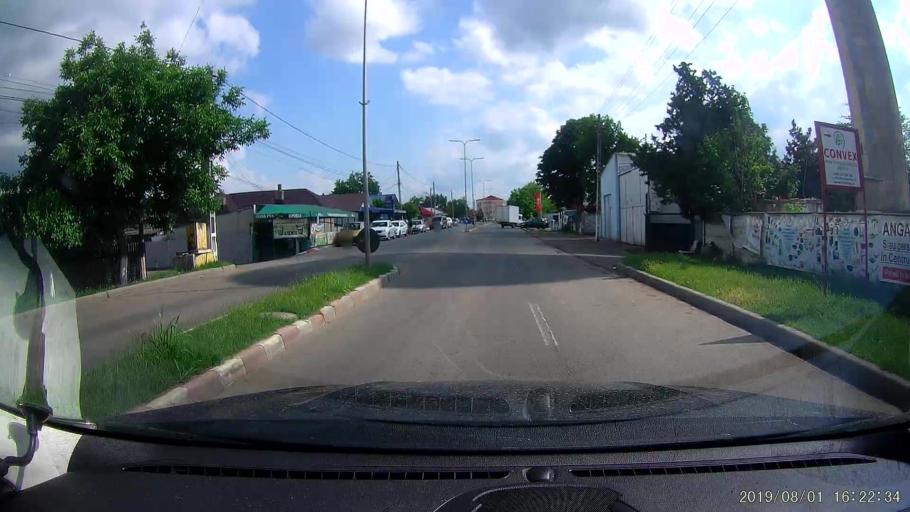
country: RO
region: Calarasi
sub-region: Municipiul Calarasi
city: Calarasi
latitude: 44.2032
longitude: 27.3375
